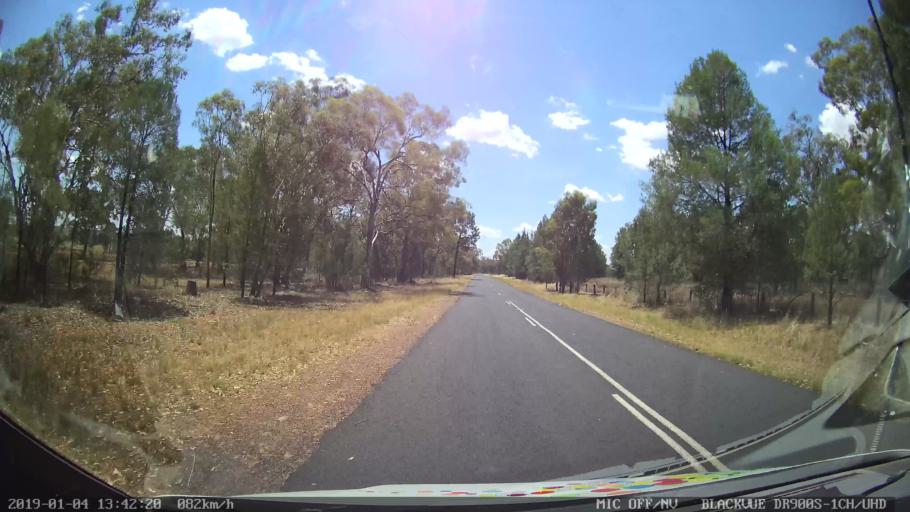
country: AU
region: New South Wales
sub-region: Dubbo Municipality
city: Dubbo
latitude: -32.4909
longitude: 148.5550
